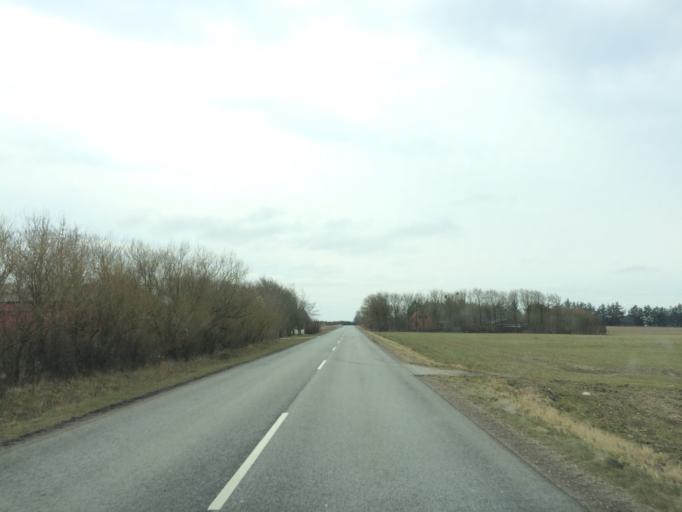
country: DK
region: Central Jutland
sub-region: Ringkobing-Skjern Kommune
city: Tarm
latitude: 55.8385
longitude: 8.4646
